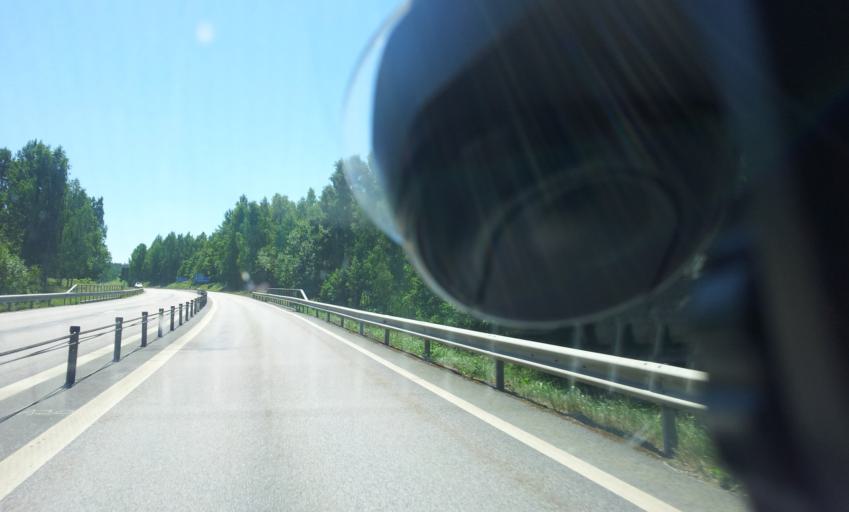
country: SE
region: Kalmar
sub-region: Vasterviks Kommun
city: Forserum
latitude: 58.0785
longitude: 16.5181
